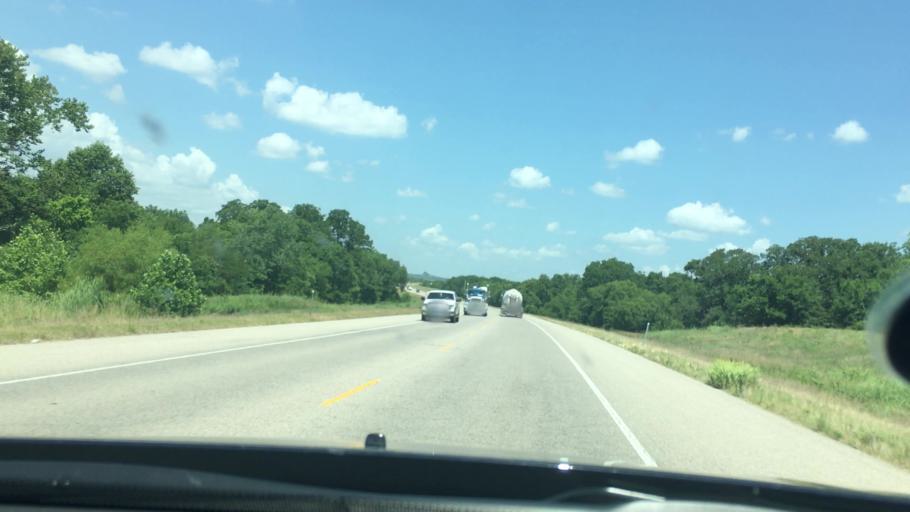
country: US
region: Oklahoma
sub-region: Pontotoc County
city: Ada
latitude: 34.7005
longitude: -96.6019
